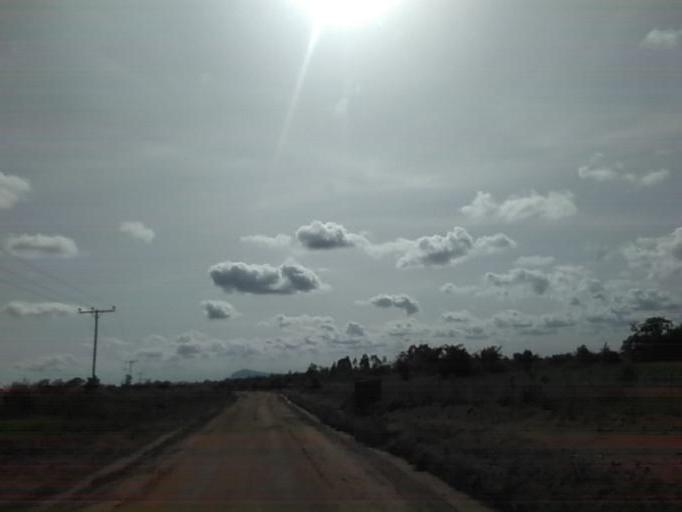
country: GH
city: Akropong
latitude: 6.0297
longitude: 0.3638
